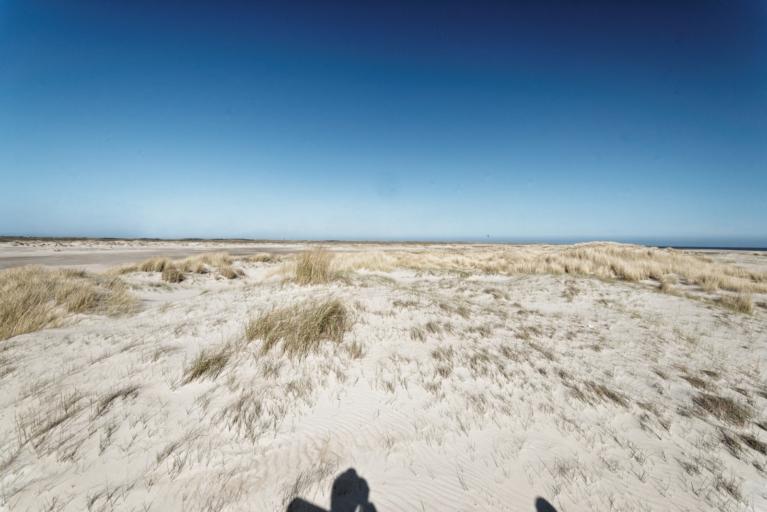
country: NL
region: North Holland
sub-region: Gemeente Den Helder
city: Den Helder
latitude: 52.9936
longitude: 4.7425
